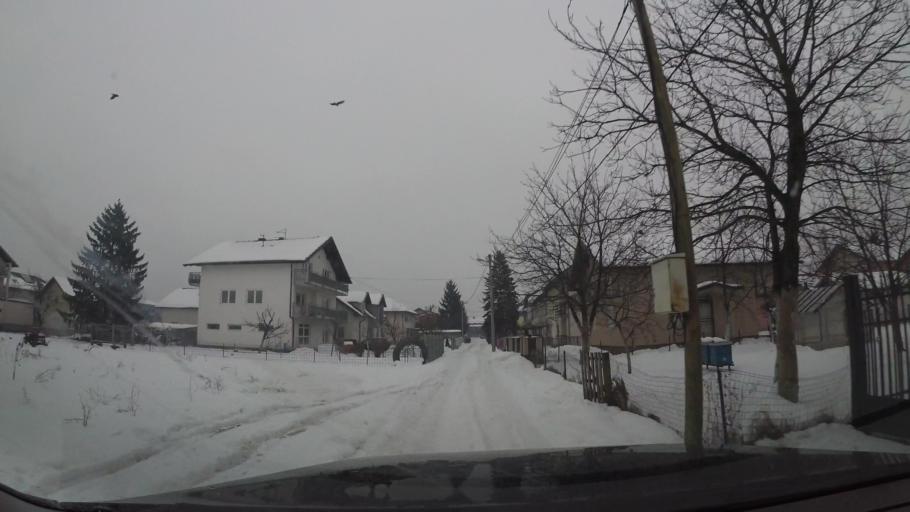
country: BA
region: Federation of Bosnia and Herzegovina
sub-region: Kanton Sarajevo
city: Sarajevo
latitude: 43.8409
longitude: 18.3000
